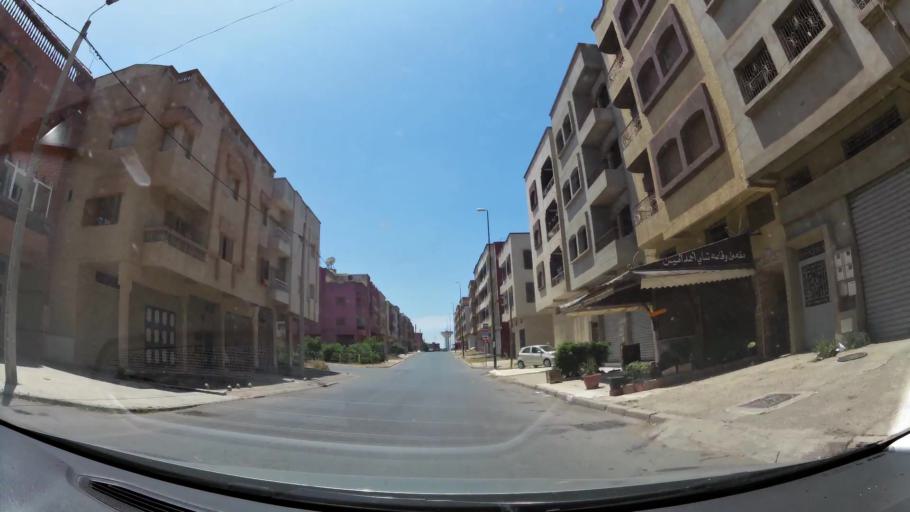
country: MA
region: Gharb-Chrarda-Beni Hssen
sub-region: Kenitra Province
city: Kenitra
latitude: 34.2605
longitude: -6.6254
